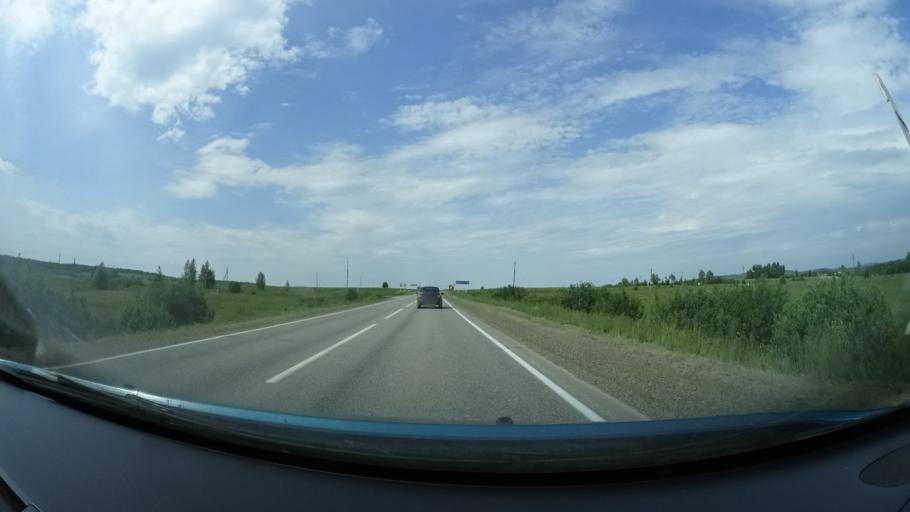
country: RU
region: Perm
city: Barda
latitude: 57.0303
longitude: 55.5505
